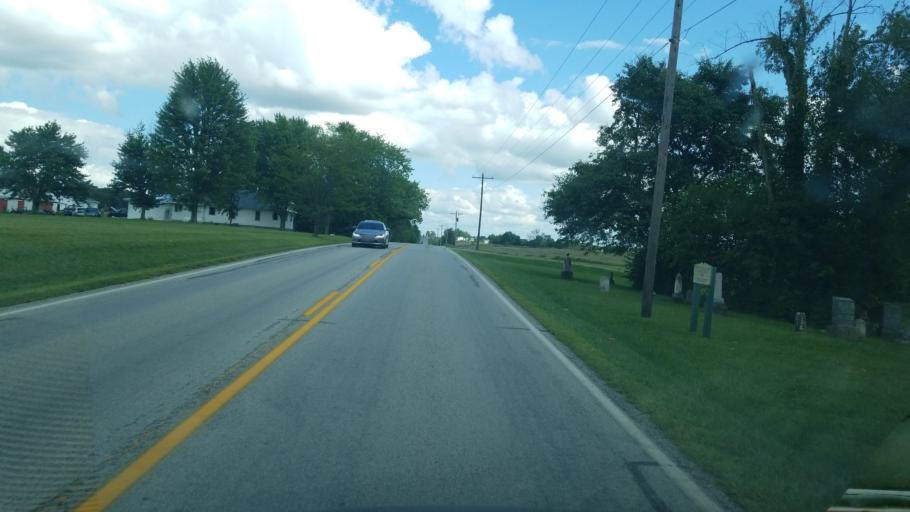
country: US
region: Ohio
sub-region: Allen County
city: Lima
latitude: 40.7888
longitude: -84.0801
